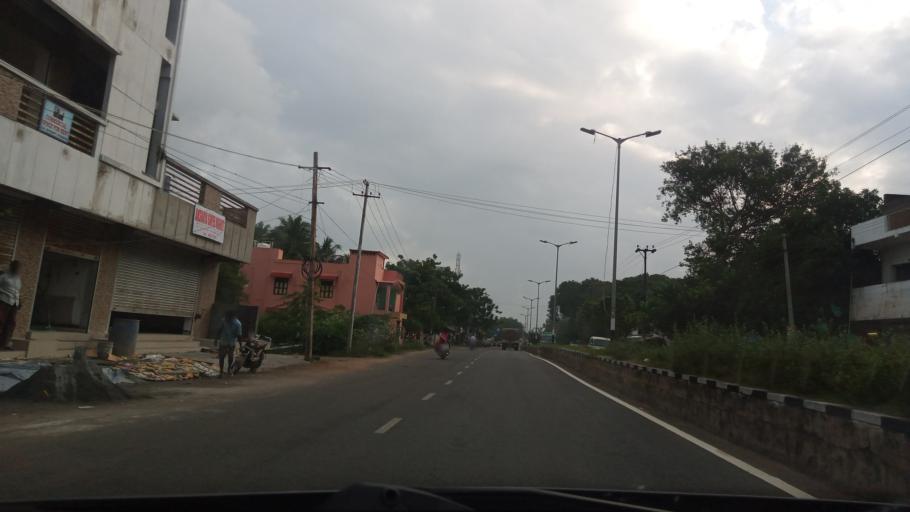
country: IN
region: Tamil Nadu
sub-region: Villupuram
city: Auroville
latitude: 12.0214
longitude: 79.8603
